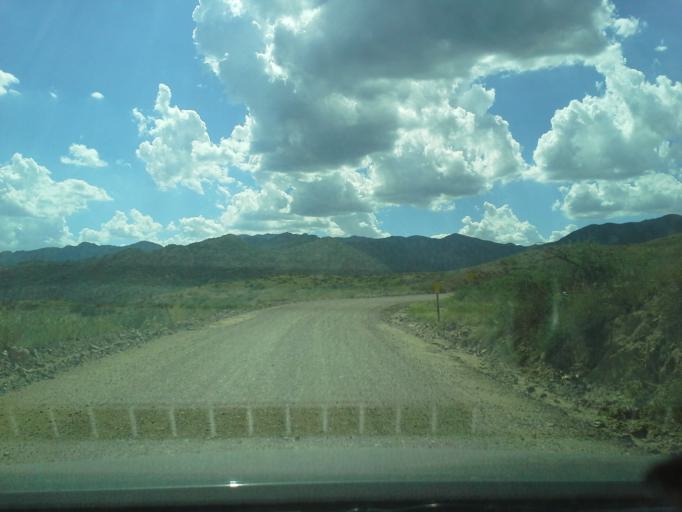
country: US
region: Arizona
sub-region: Yavapai County
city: Spring Valley
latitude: 34.2775
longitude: -112.2381
